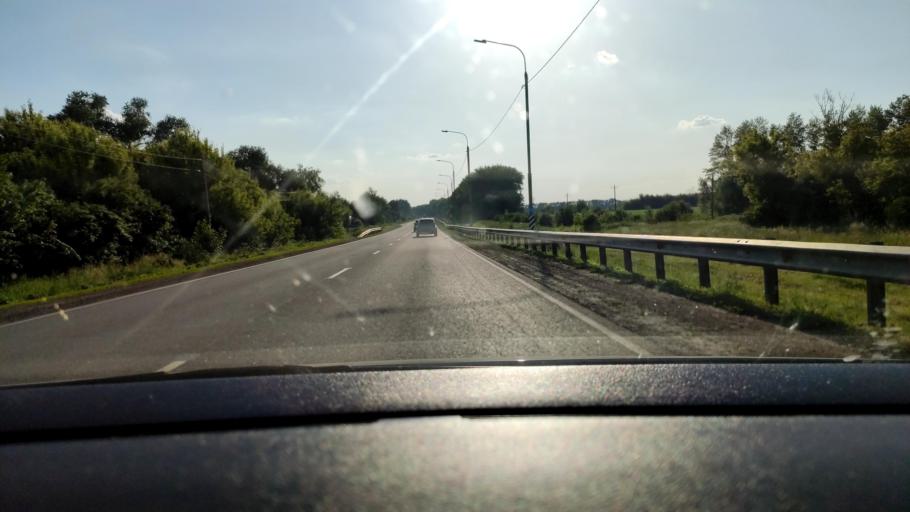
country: RU
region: Voronezj
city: Kashirskoye
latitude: 51.4584
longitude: 39.8088
